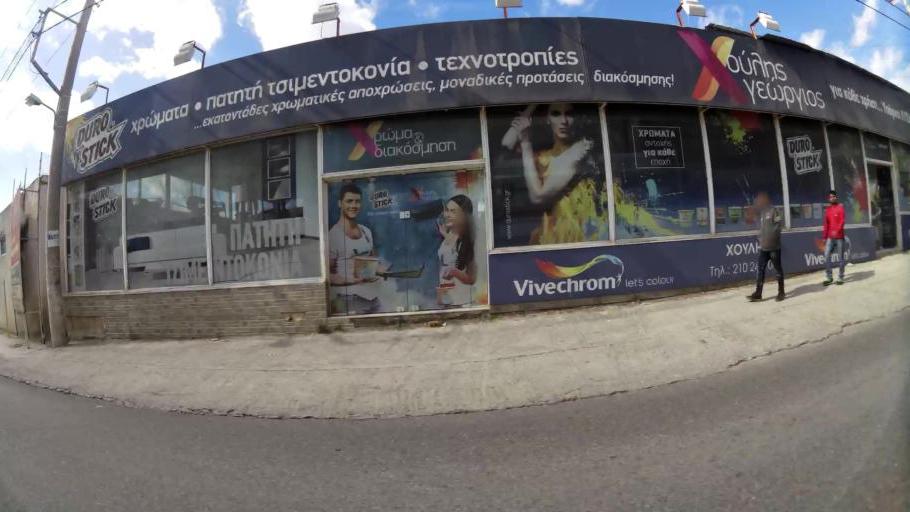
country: GR
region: Attica
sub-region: Nomarchia Anatolikis Attikis
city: Acharnes
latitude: 38.1047
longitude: 23.7430
